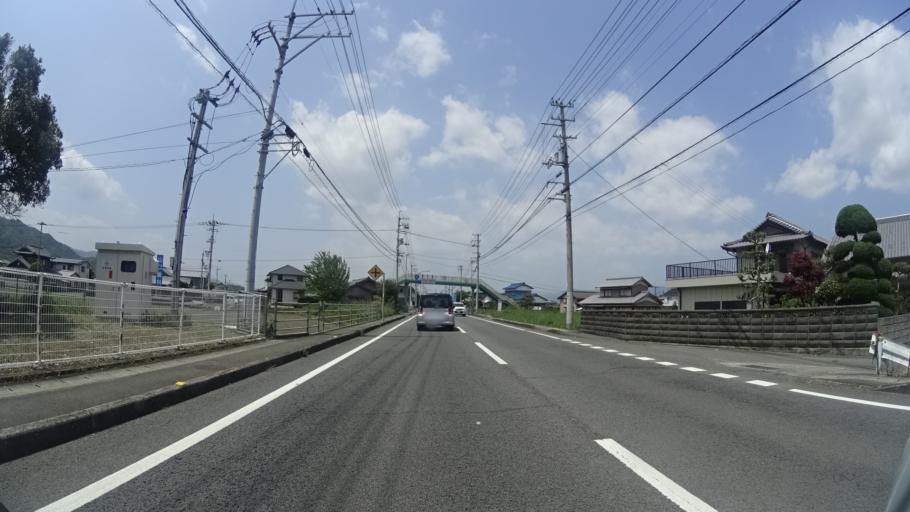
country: JP
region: Tokushima
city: Ishii
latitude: 34.0682
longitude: 134.4136
